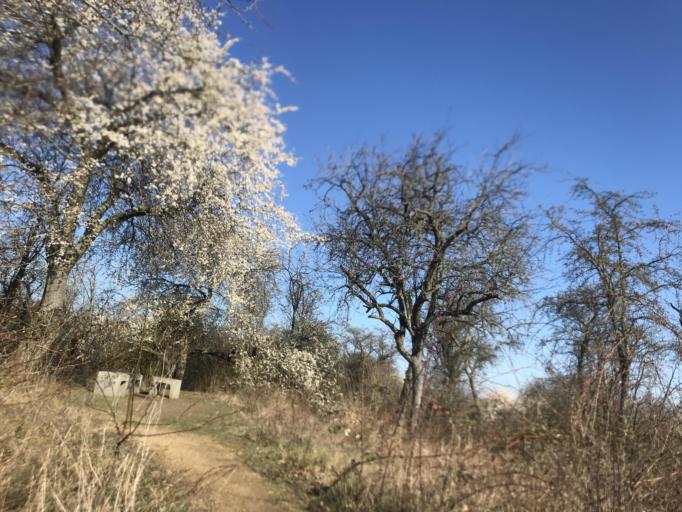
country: DE
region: Hesse
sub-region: Regierungsbezirk Darmstadt
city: Florsheim
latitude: 50.0103
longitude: 8.4044
